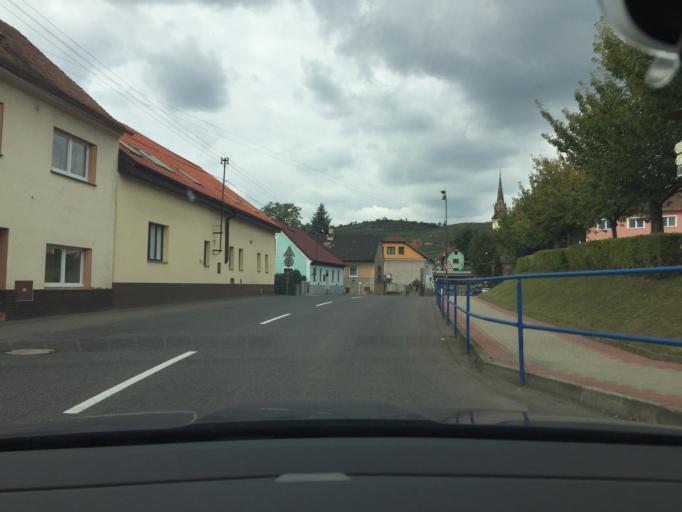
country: CZ
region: Ustecky
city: Lovosice
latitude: 50.5378
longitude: 14.0643
